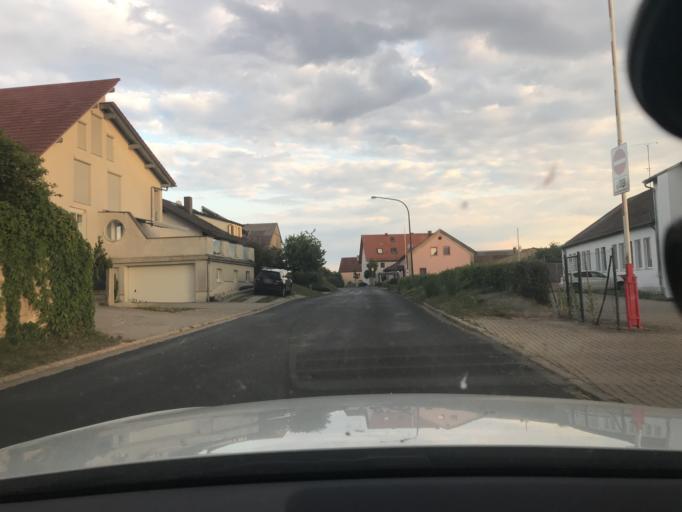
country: DE
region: Bavaria
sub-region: Upper Palatinate
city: Auerbach
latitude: 49.7359
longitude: 11.6103
